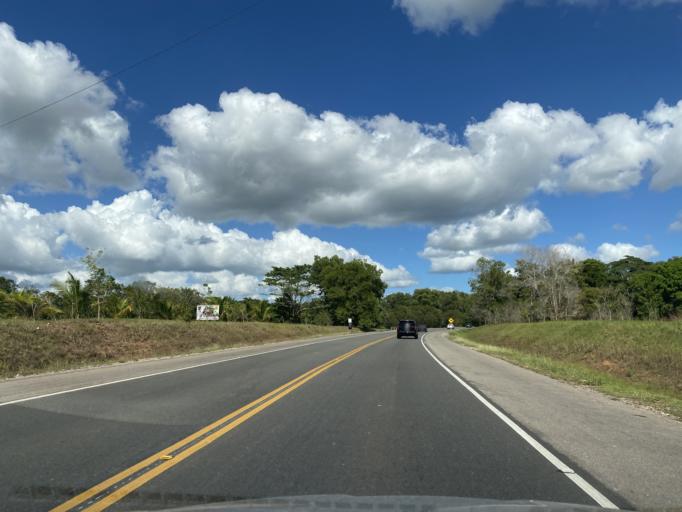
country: DO
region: Monte Plata
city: Monte Plata
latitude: 18.7592
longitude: -69.7641
